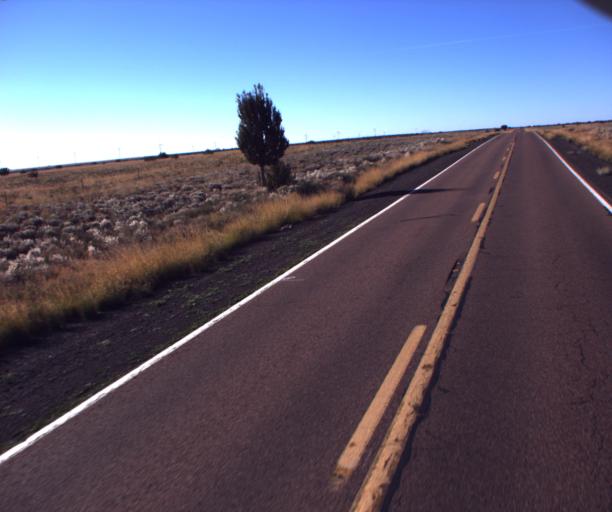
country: US
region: Arizona
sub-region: Navajo County
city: Holbrook
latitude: 34.7164
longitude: -110.2963
